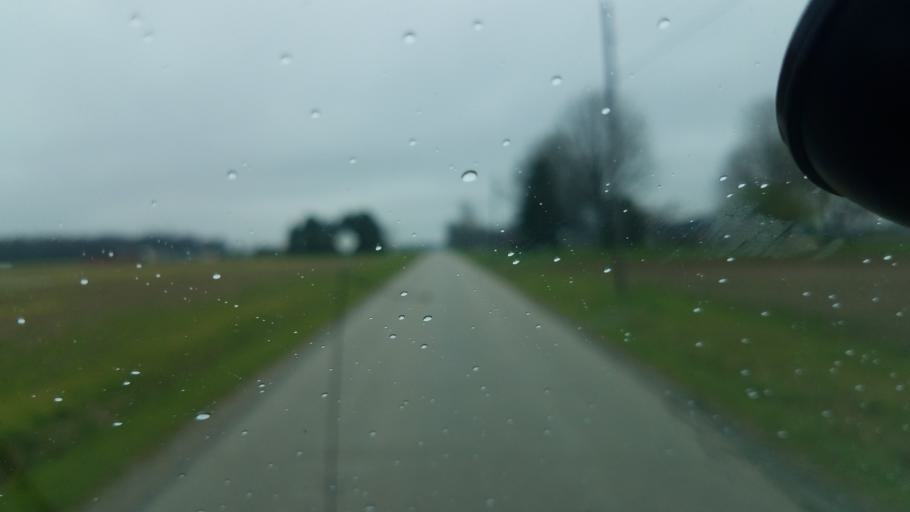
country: US
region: Ohio
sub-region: Crawford County
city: Galion
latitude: 40.7711
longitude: -82.8568
